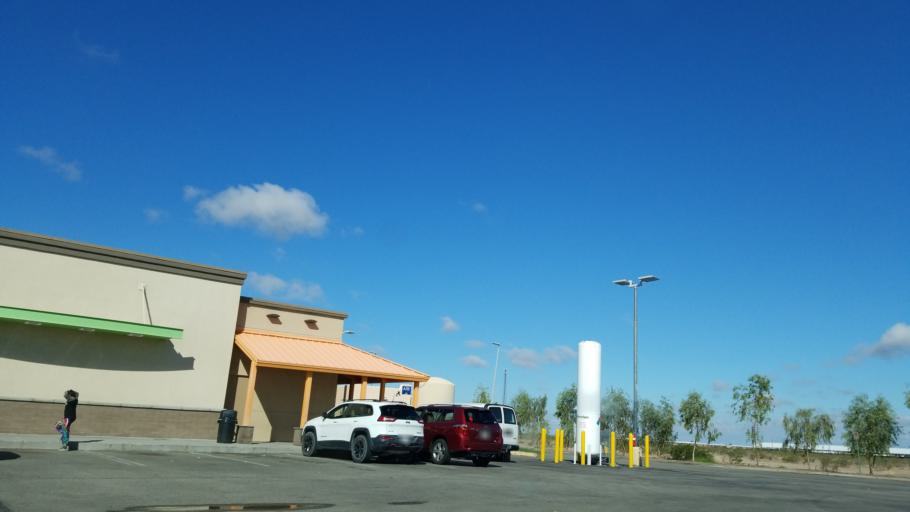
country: US
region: Arizona
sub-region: La Paz County
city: Salome
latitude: 33.6344
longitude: -113.7680
